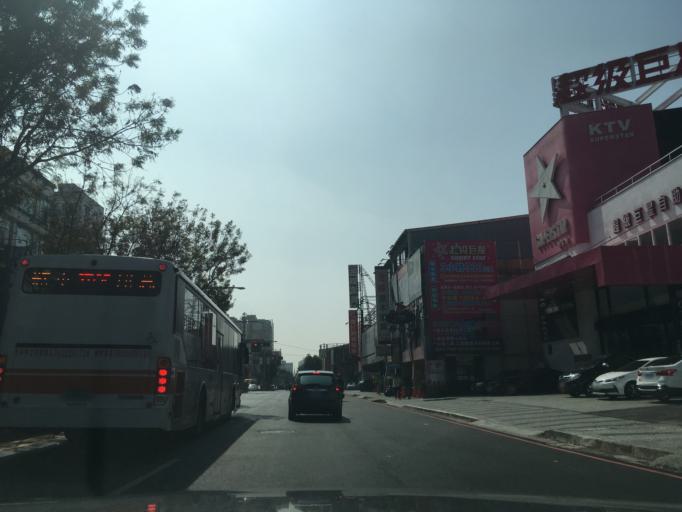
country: TW
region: Taiwan
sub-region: Taichung City
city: Taichung
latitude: 24.1903
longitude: 120.6613
